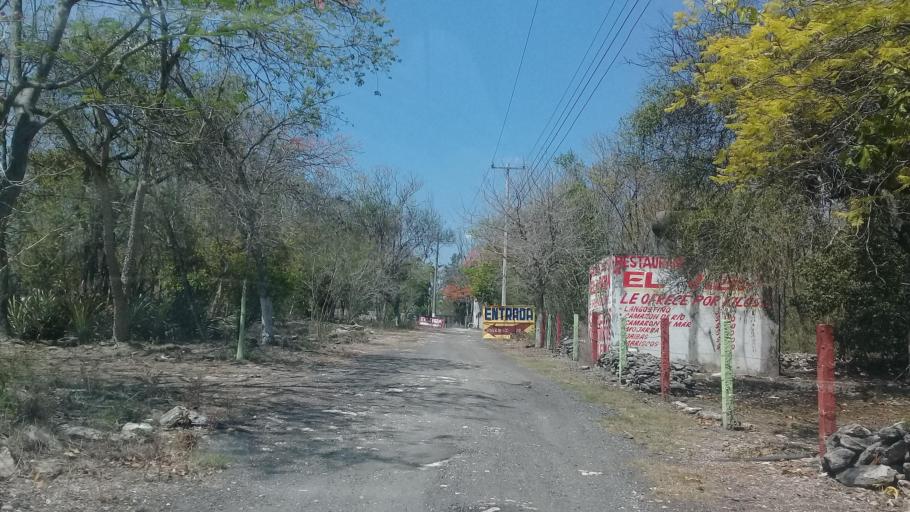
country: MX
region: Veracruz
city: Rinconada
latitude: 19.3804
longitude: -96.5990
